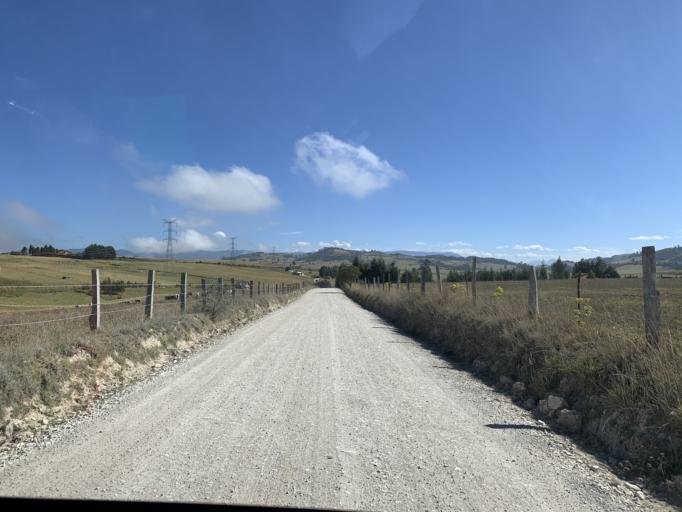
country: CO
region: Boyaca
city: Tuta
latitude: 5.6658
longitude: -73.1505
